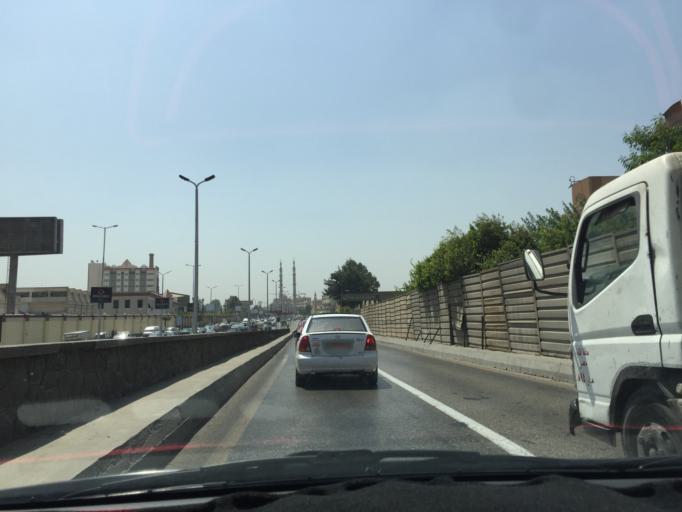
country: EG
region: Muhafazat al Qahirah
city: Cairo
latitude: 30.0675
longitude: 31.2898
